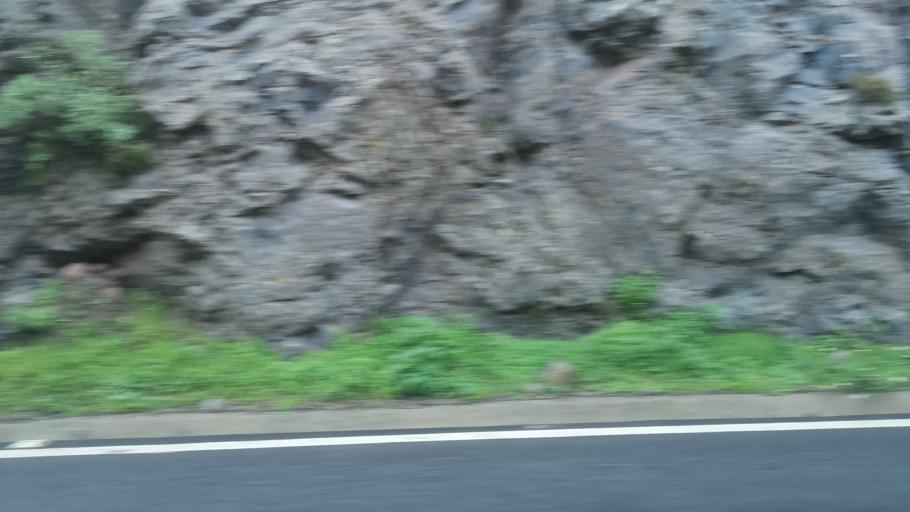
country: ES
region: Canary Islands
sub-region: Provincia de Santa Cruz de Tenerife
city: Alajero
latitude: 28.1003
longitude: -17.2048
